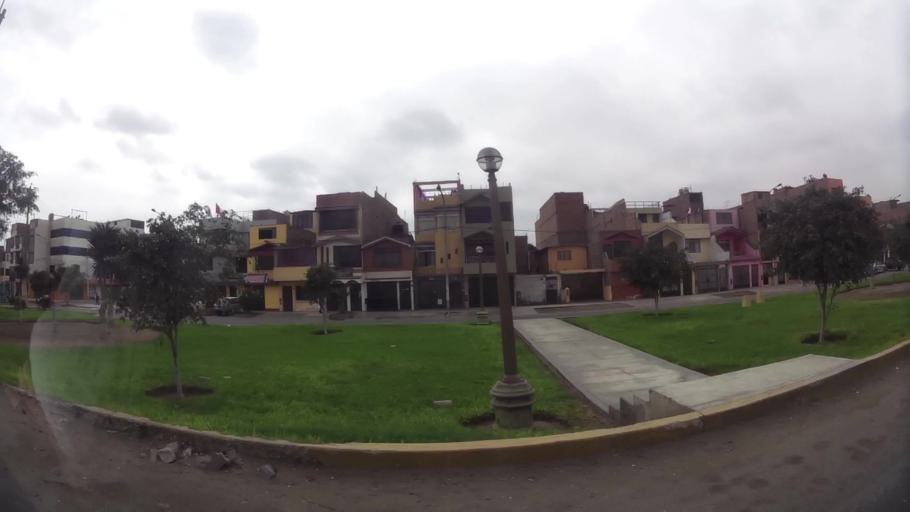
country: PE
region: Callao
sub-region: Callao
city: Callao
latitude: -11.9981
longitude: -77.1166
